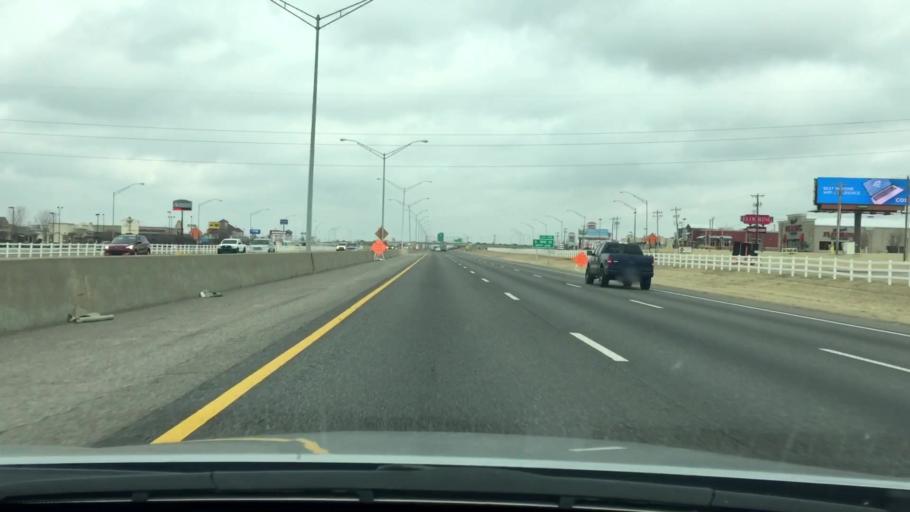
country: US
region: Oklahoma
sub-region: Cleveland County
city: Moore
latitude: 35.3116
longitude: -97.4899
